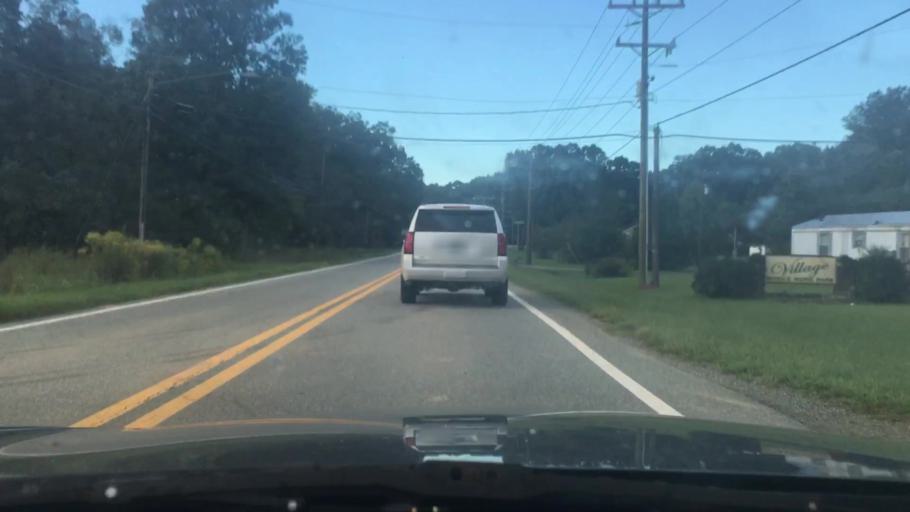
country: US
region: North Carolina
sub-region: Alamance County
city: Green Level
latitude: 36.1333
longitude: -79.3449
